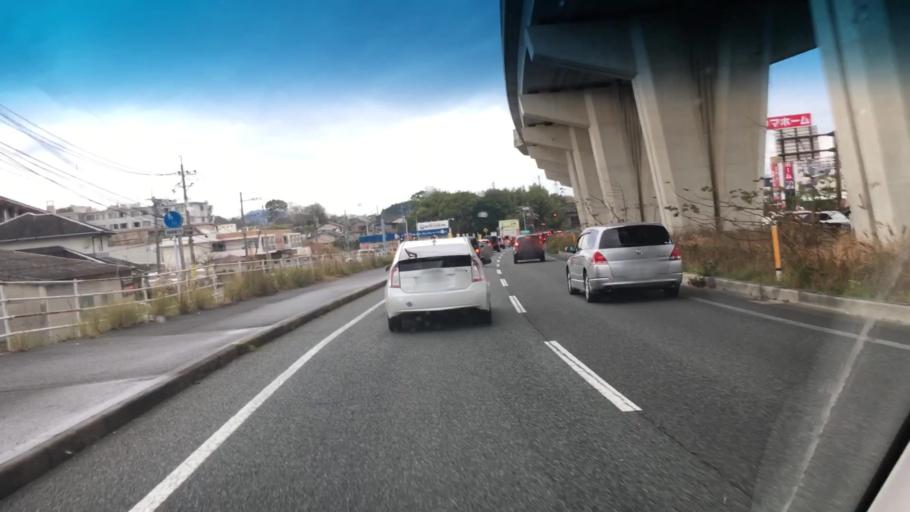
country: JP
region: Fukuoka
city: Maebaru-chuo
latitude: 33.5724
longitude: 130.2700
